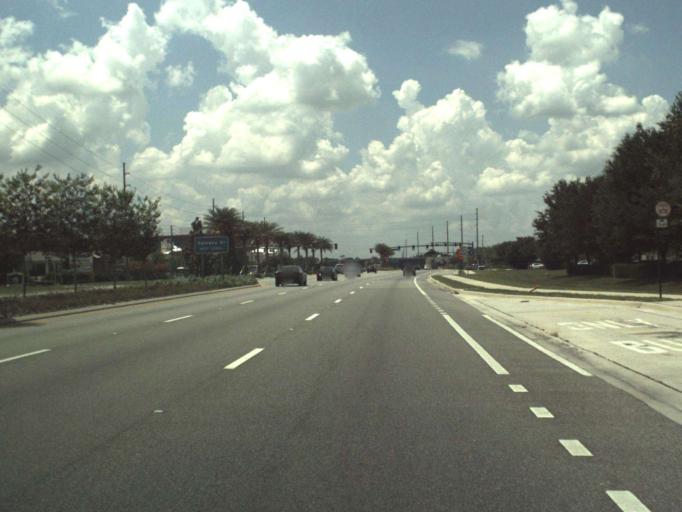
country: US
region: Florida
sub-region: Seminole County
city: Forest City
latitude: 28.6469
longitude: -81.4154
